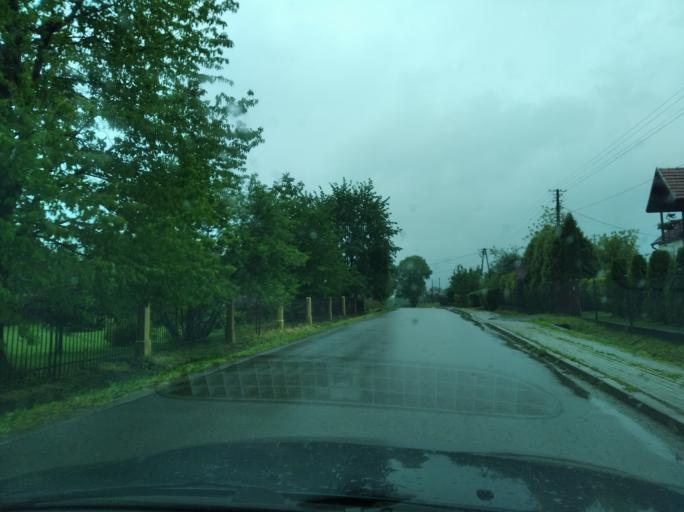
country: PL
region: Subcarpathian Voivodeship
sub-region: Powiat jasielski
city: Tarnowiec
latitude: 49.7644
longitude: 21.5402
